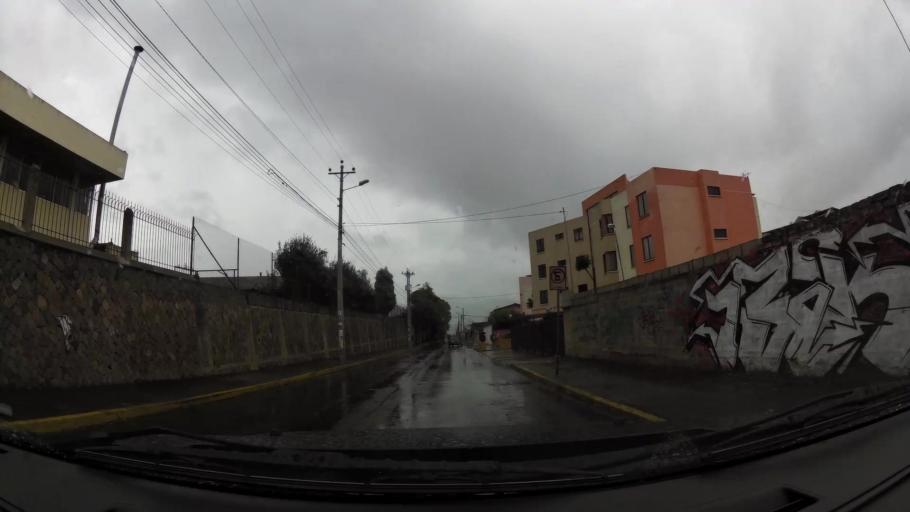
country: EC
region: Pichincha
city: Quito
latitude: -0.1208
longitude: -78.4969
